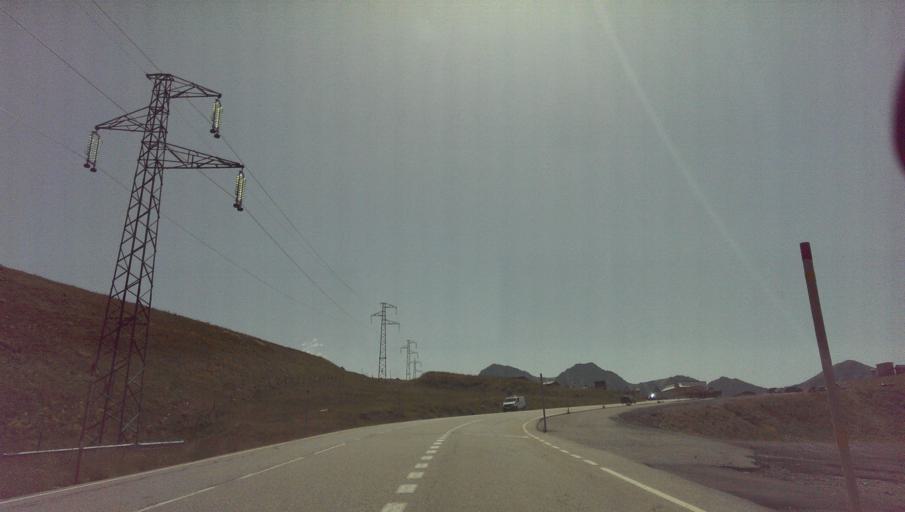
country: AD
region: Encamp
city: Pas de la Casa
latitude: 42.5416
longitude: 1.7178
